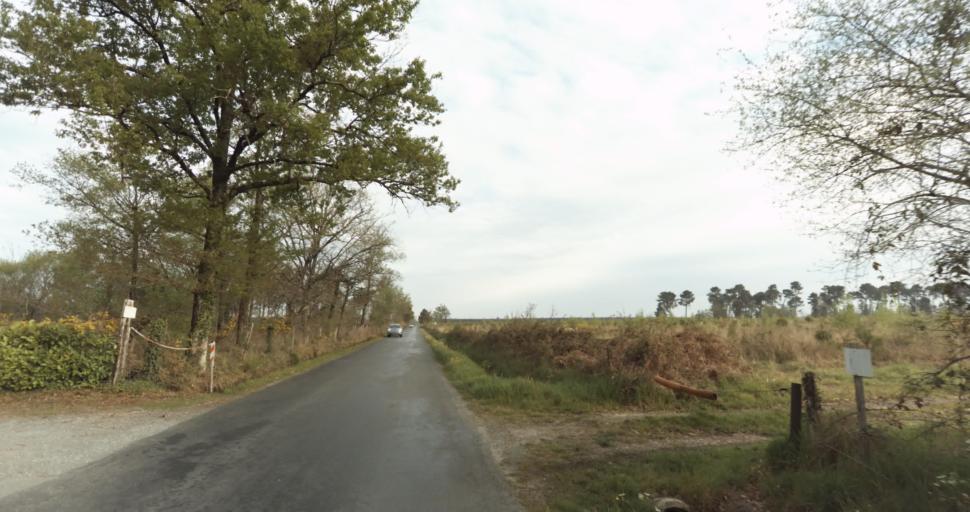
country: FR
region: Aquitaine
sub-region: Departement de la Gironde
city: Saint-Aubin-de-Medoc
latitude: 44.7791
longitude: -0.7443
